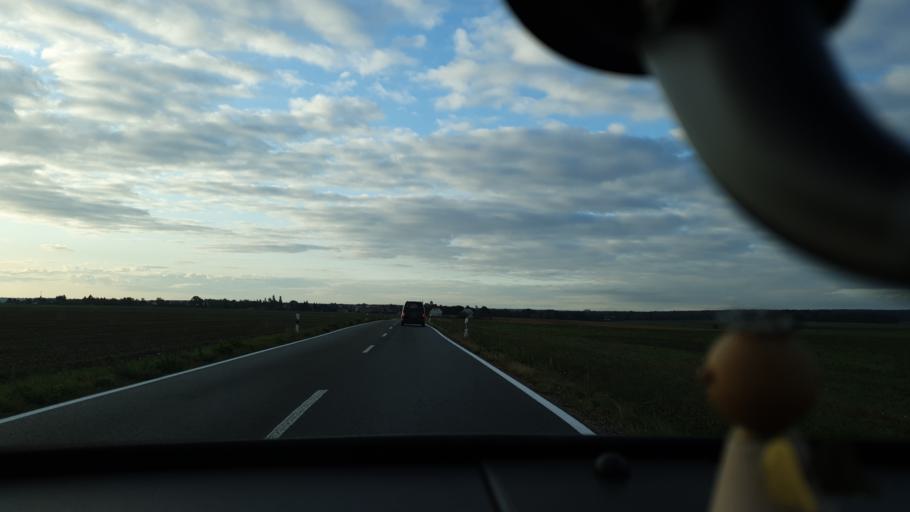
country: DE
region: Saxony
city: Schildau
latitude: 51.4706
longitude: 12.9253
